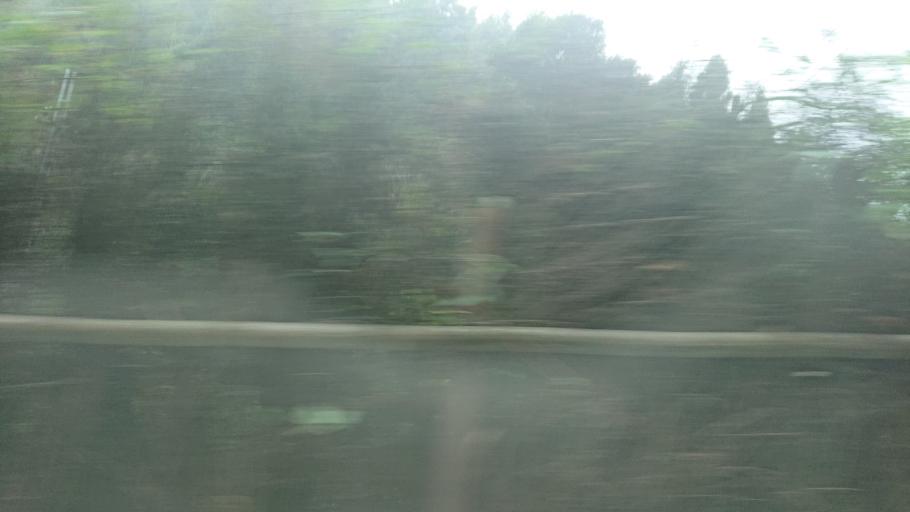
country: TW
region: Taiwan
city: Lugu
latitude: 23.6245
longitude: 120.7122
